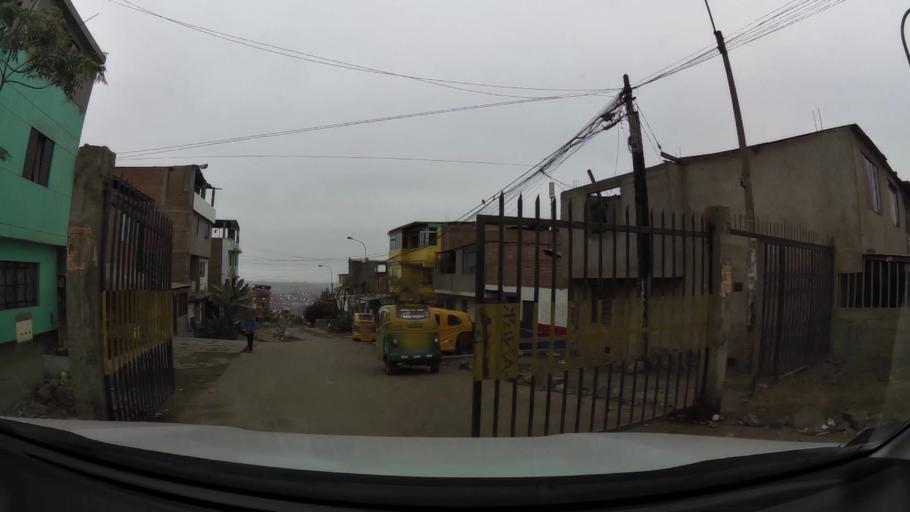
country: PE
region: Lima
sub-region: Lima
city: Surco
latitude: -12.1750
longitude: -76.9563
